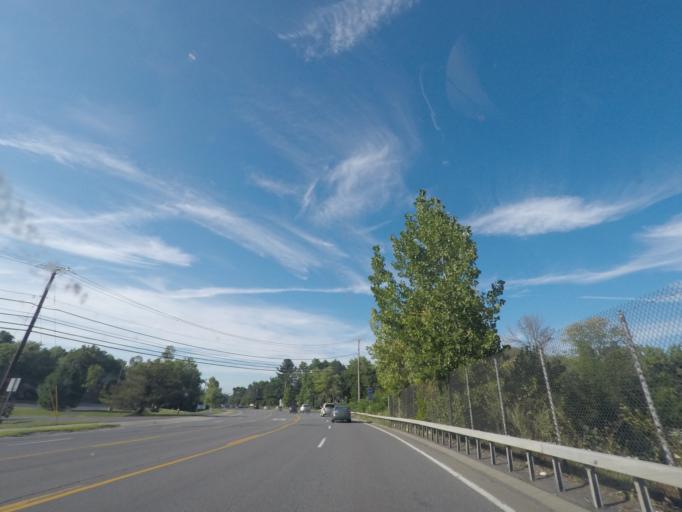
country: US
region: New York
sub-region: Schenectady County
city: Niskayuna
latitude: 42.7608
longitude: -73.8140
